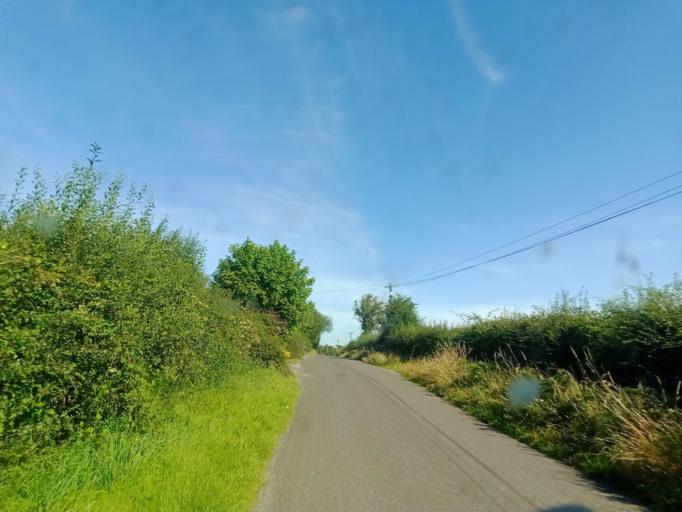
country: IE
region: Leinster
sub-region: Kilkenny
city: Ballyragget
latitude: 52.7674
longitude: -7.4097
